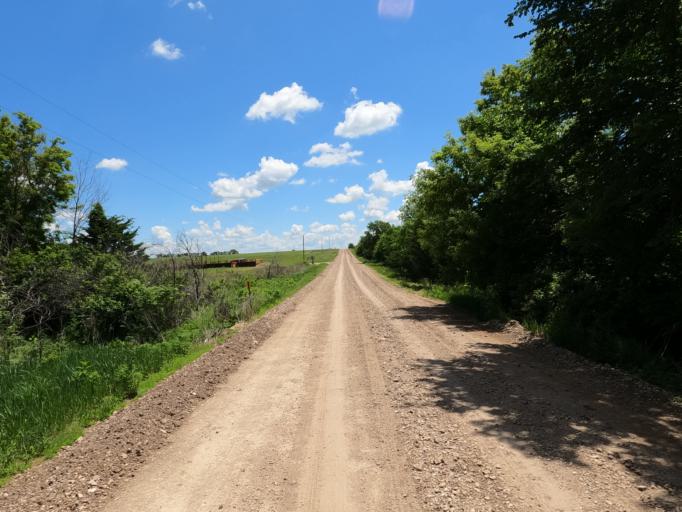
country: US
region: Kansas
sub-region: Marion County
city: Marion
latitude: 38.2164
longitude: -96.7845
